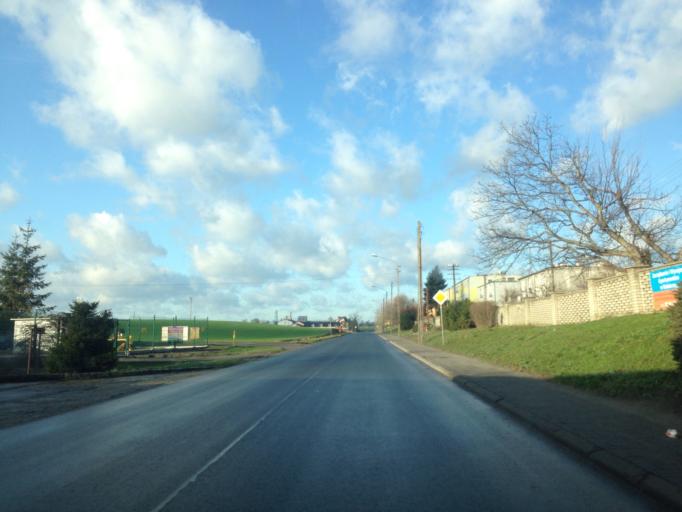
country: PL
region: Kujawsko-Pomorskie
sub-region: Powiat grudziadzki
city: Lasin
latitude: 53.5255
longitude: 19.0813
